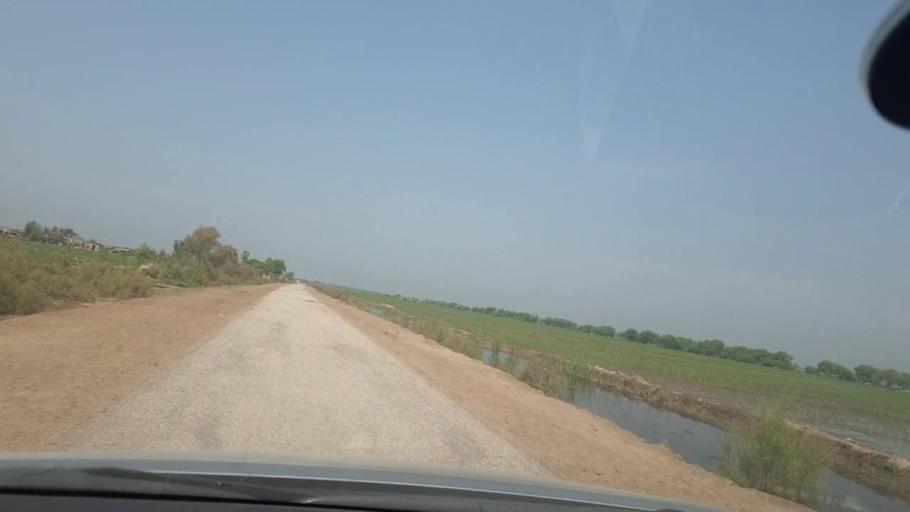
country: PK
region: Balochistan
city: Mehrabpur
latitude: 28.0654
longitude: 68.0613
